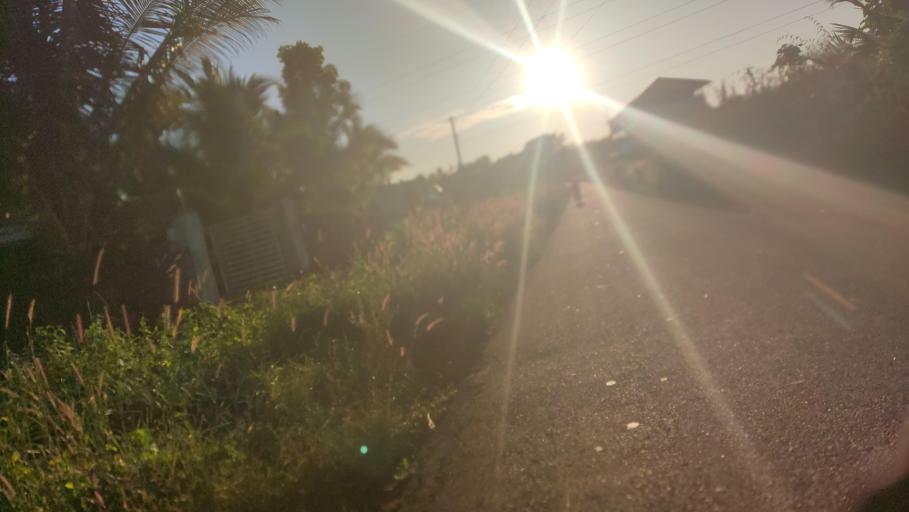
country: IN
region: Kerala
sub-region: Kasaragod District
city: Kannangad
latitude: 12.4171
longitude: 75.0981
